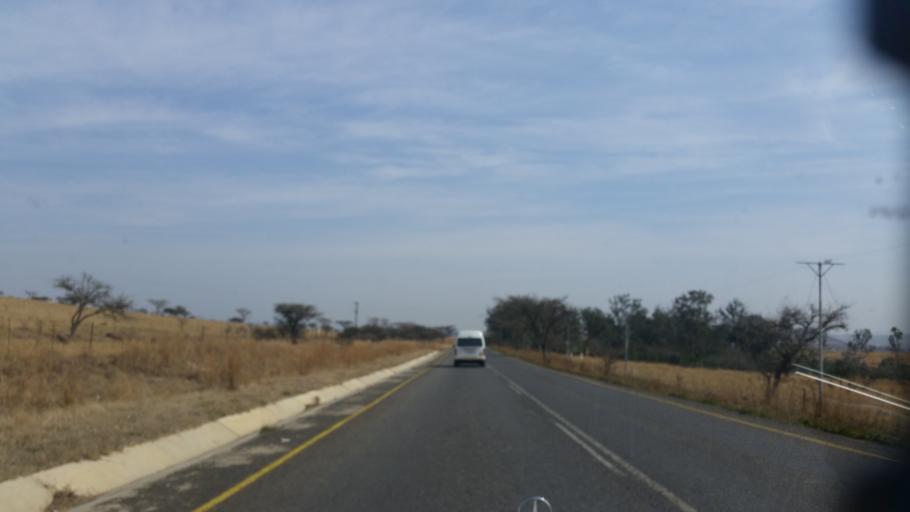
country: ZA
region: KwaZulu-Natal
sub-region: uThukela District Municipality
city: Estcourt
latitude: -29.0563
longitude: 29.9286
